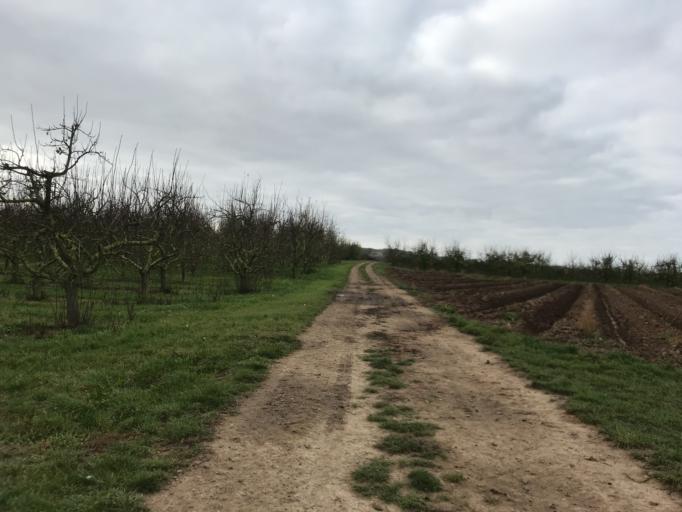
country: DE
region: Rheinland-Pfalz
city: Budenheim
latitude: 49.9801
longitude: 8.1579
